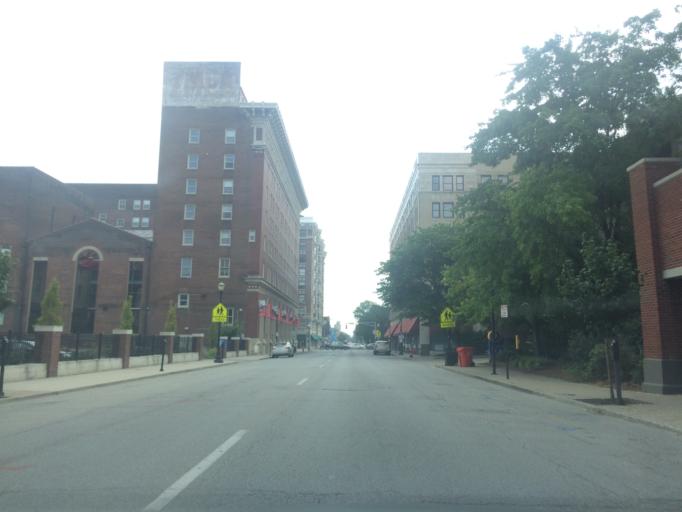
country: US
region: Kentucky
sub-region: Jefferson County
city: Louisville
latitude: 38.2473
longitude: -85.7566
